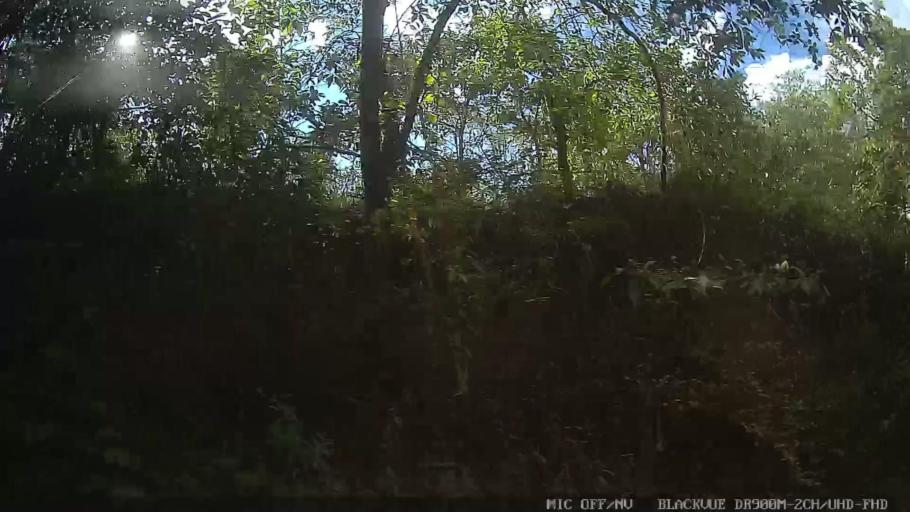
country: BR
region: Sao Paulo
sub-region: Bom Jesus Dos Perdoes
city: Bom Jesus dos Perdoes
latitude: -23.1387
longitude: -46.5088
